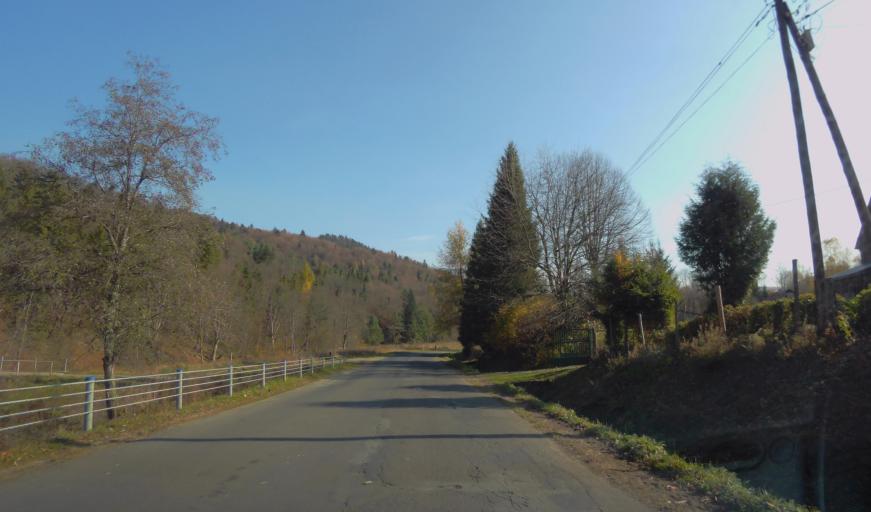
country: PL
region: Subcarpathian Voivodeship
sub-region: Powiat leski
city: Cisna
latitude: 49.2095
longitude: 22.2699
